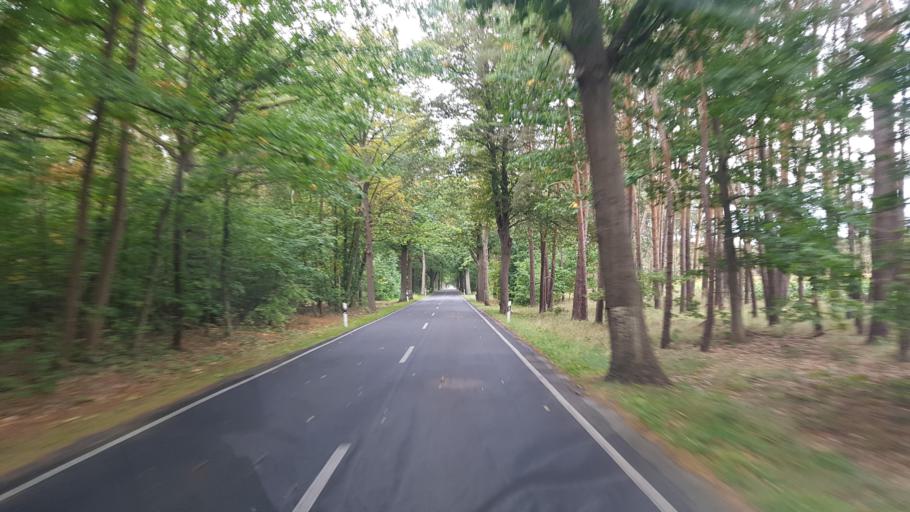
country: DE
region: Brandenburg
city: Kasel-Golzig
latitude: 51.9349
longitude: 13.6833
